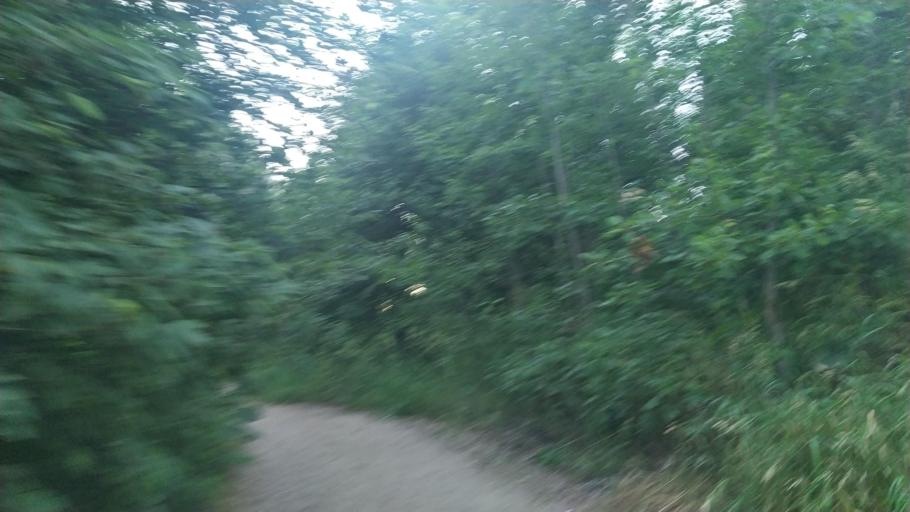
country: RU
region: St.-Petersburg
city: Kronshtadt
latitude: 60.0246
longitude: 29.6727
